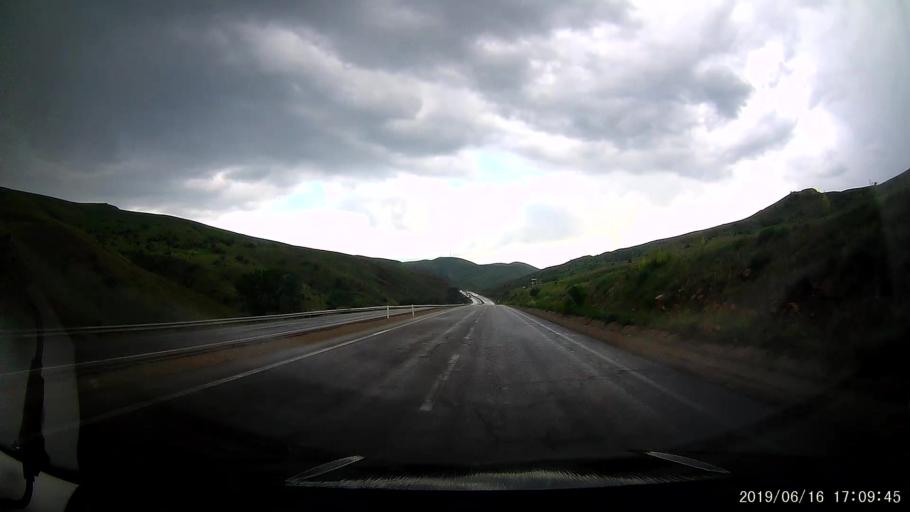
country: TR
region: Erzurum
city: Askale
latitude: 39.8901
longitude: 40.6479
